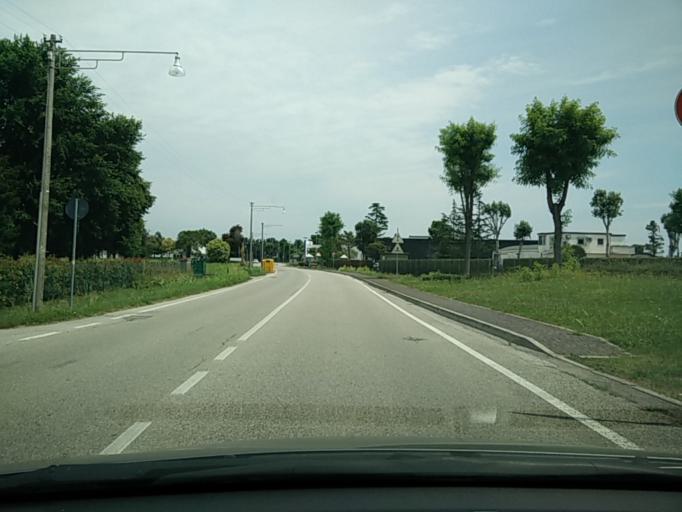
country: IT
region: Veneto
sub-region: Provincia di Venezia
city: San Liberale
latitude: 45.5191
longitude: 12.3568
